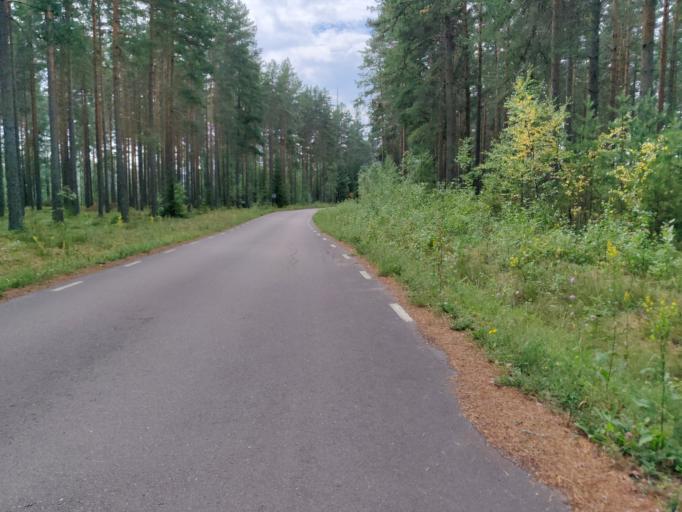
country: SE
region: Vaermland
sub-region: Munkfors Kommun
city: Munkfors
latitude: 59.9608
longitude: 13.5328
